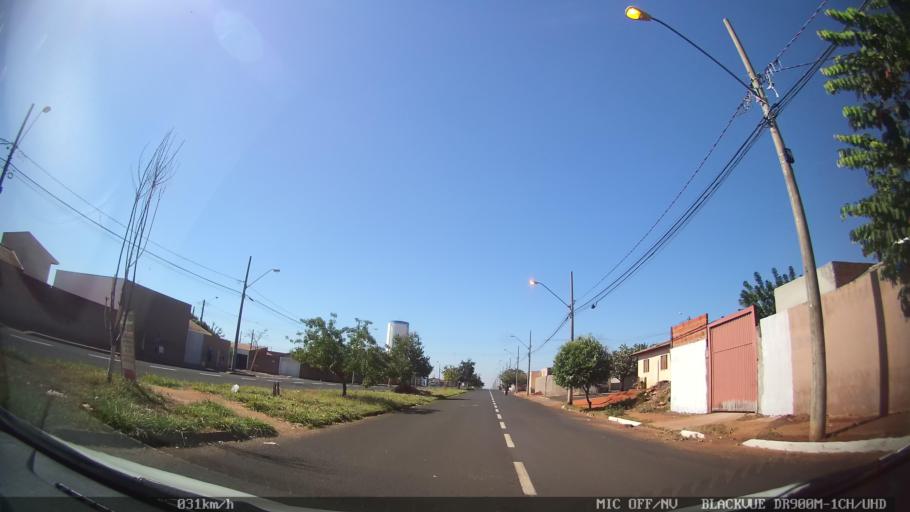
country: BR
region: Sao Paulo
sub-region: Sao Jose Do Rio Preto
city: Sao Jose do Rio Preto
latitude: -20.7405
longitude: -49.4174
